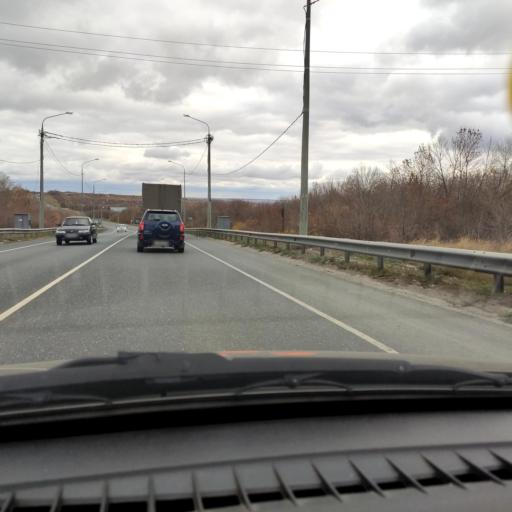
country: RU
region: Samara
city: Mezhdurechensk
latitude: 53.2475
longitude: 49.0140
